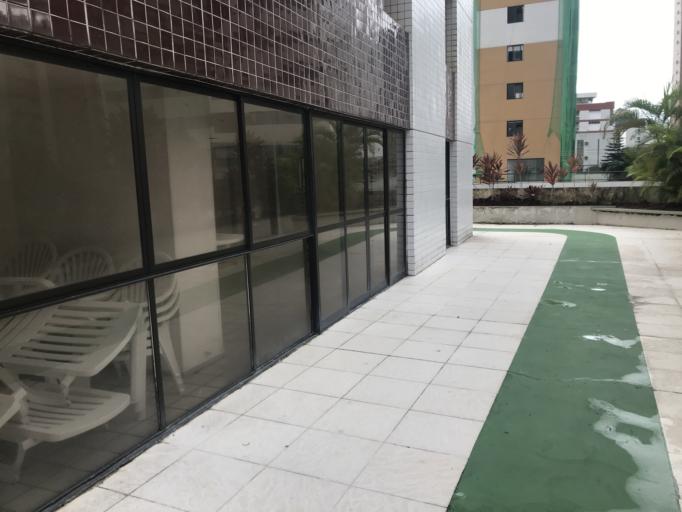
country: BR
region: Pernambuco
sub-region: Recife
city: Recife
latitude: -8.0303
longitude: -34.9090
